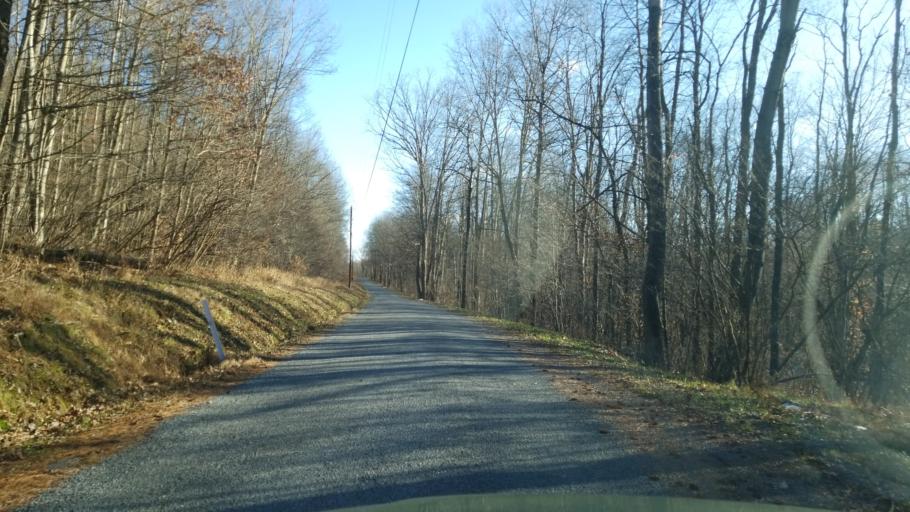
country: US
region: Pennsylvania
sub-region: Jefferson County
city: Brockway
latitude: 41.2763
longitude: -78.8159
